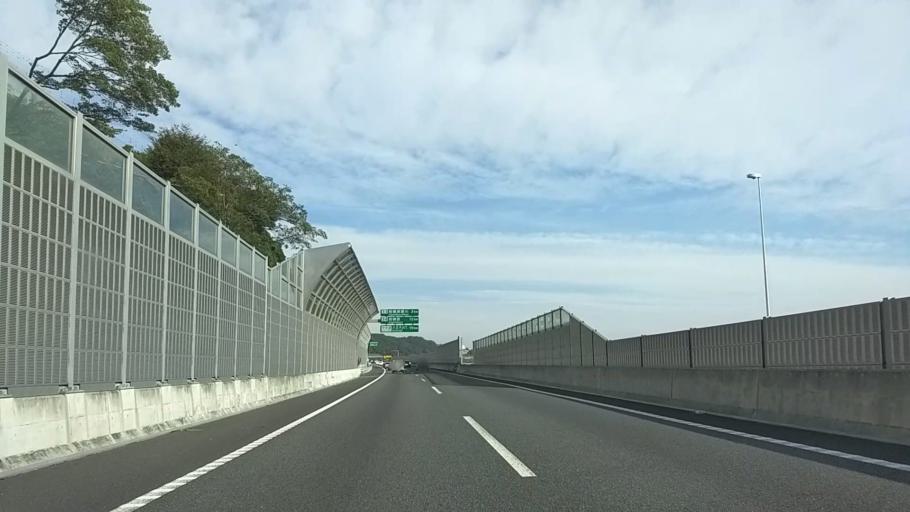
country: JP
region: Kanagawa
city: Zama
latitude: 35.4940
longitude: 139.3678
